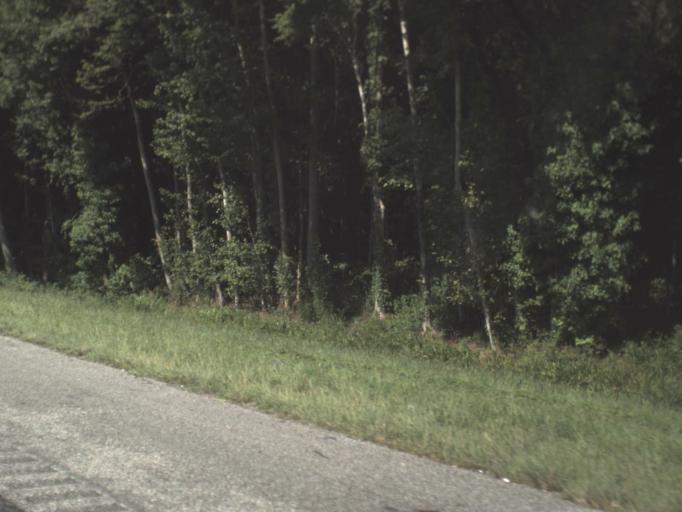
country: US
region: Florida
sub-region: Saint Johns County
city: Palm Valley
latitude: 30.0873
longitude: -81.4980
